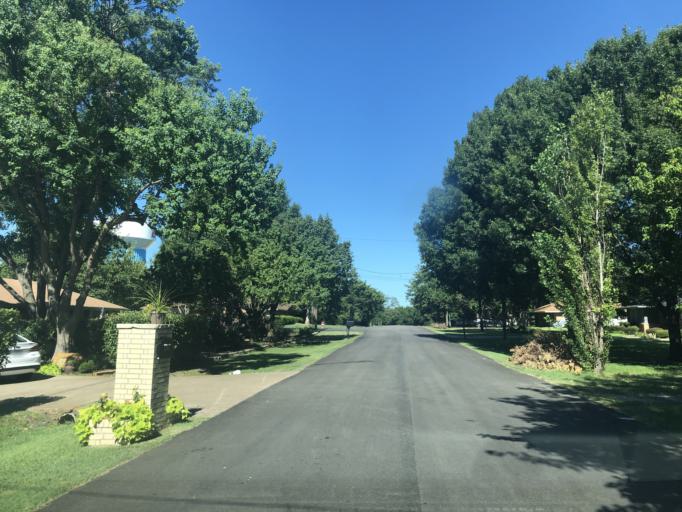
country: US
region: Texas
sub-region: Dallas County
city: Duncanville
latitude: 32.6510
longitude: -96.9395
